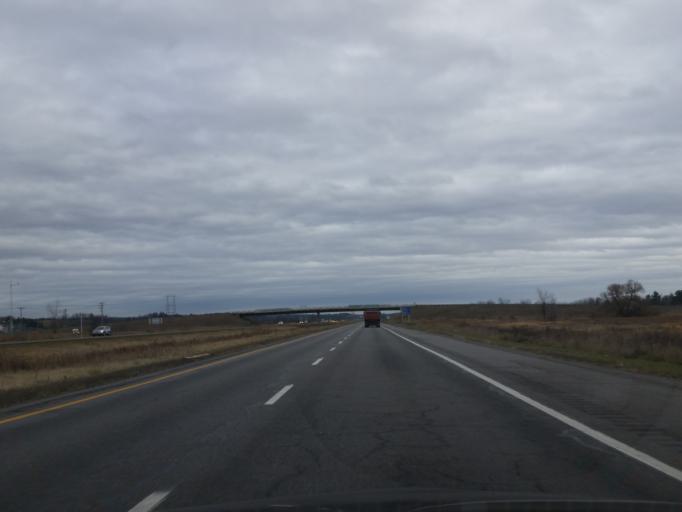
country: CA
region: Quebec
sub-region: Outaouais
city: Gatineau
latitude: 45.5202
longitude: -75.5327
